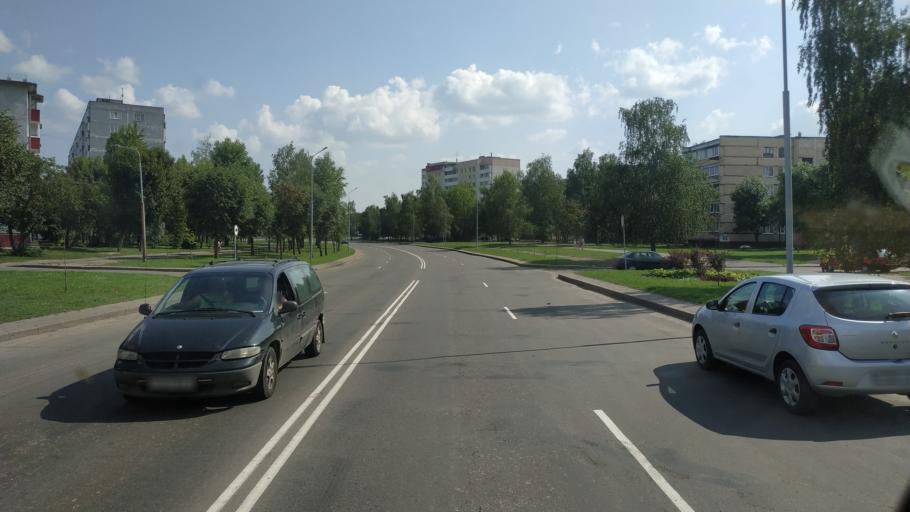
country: BY
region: Mogilev
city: Buynichy
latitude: 53.8689
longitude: 30.3138
